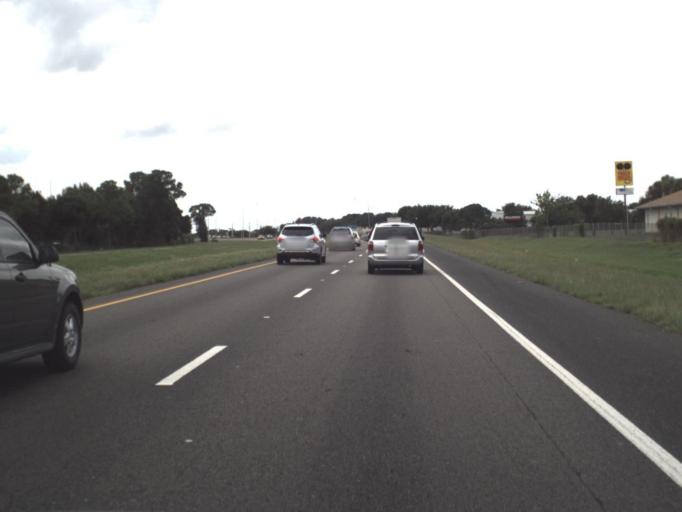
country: US
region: Florida
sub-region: Manatee County
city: Whitfield
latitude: 27.4239
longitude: -82.5317
